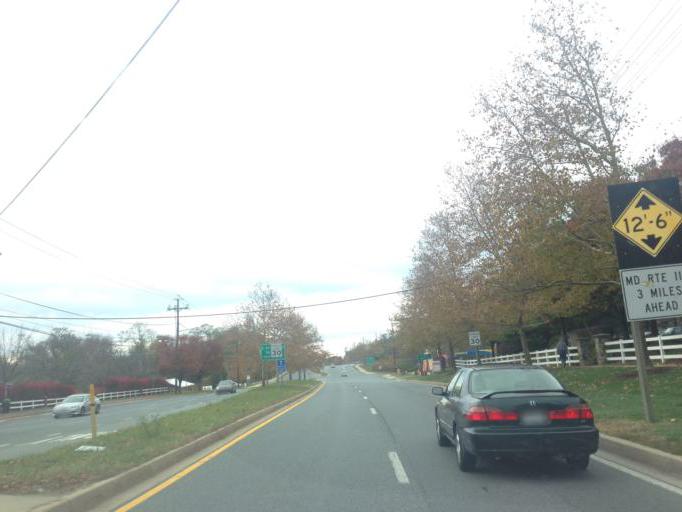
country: US
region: Maryland
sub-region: Montgomery County
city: Germantown
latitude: 39.1610
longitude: -77.2794
